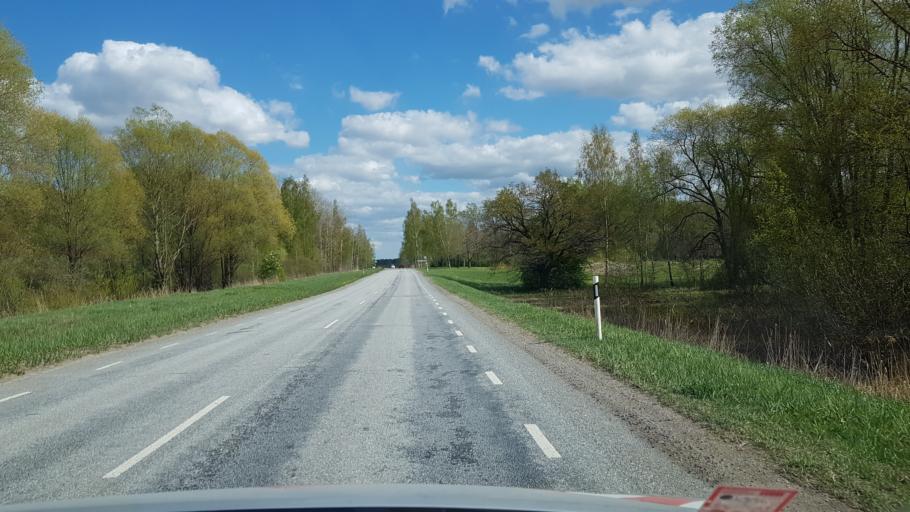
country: EE
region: Tartu
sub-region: UElenurme vald
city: Ulenurme
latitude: 58.3293
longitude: 26.7389
